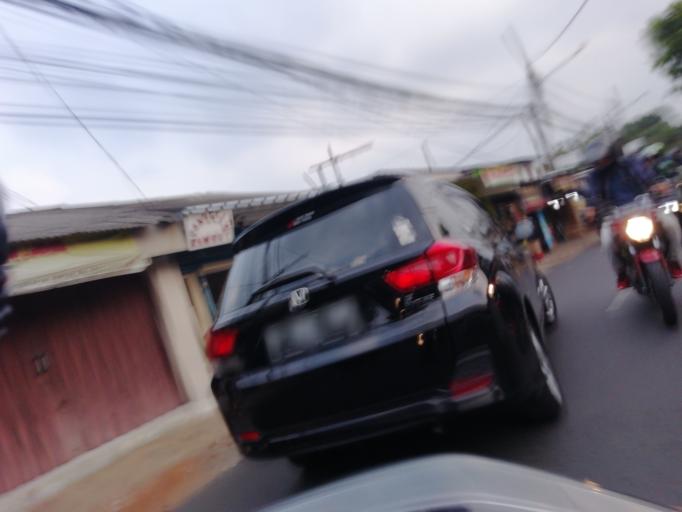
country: ID
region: West Java
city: Depok
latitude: -6.3363
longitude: 106.8307
